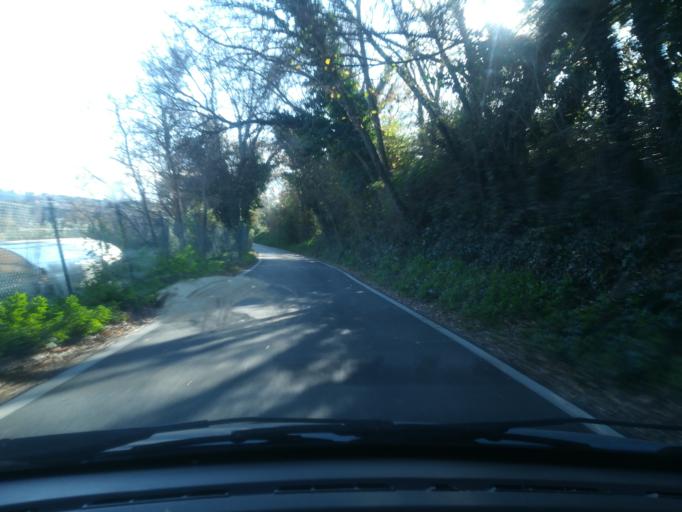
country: IT
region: The Marches
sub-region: Provincia di Macerata
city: Macerata
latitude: 43.2944
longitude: 13.4406
